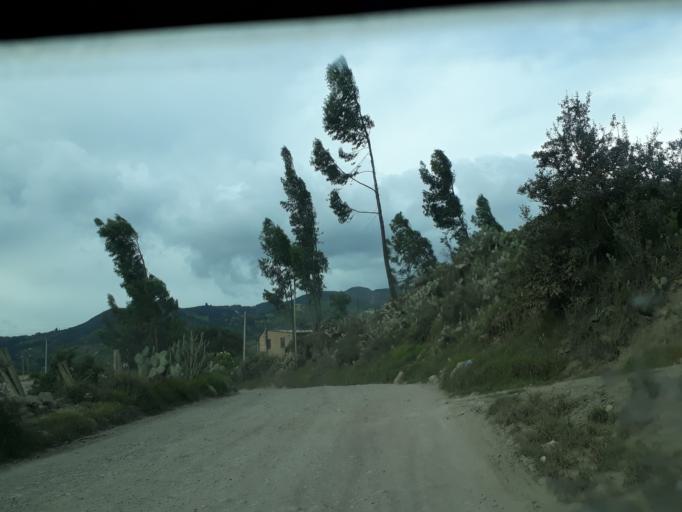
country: CO
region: Cundinamarca
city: Cucunuba
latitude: 5.2513
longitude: -73.7825
